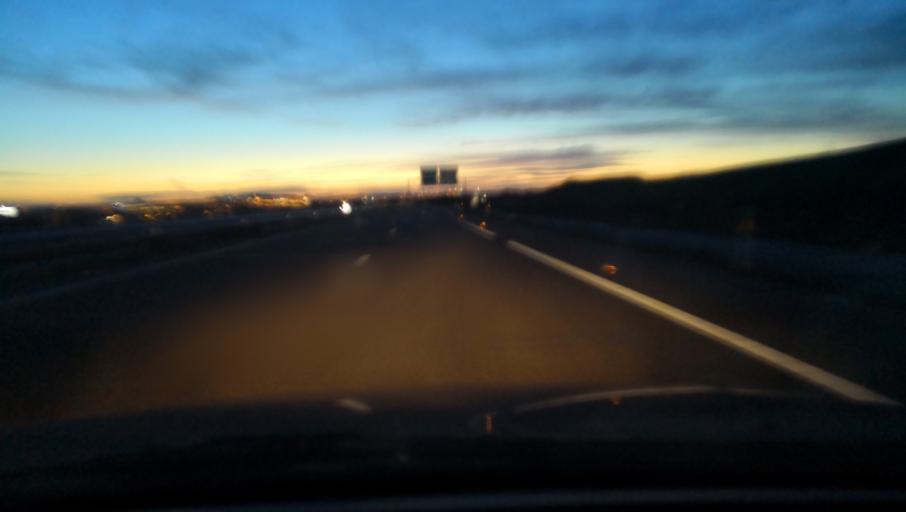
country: ES
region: Castille and Leon
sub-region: Provincia de Zamora
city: Monfarracinos
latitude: 41.5336
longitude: -5.6914
